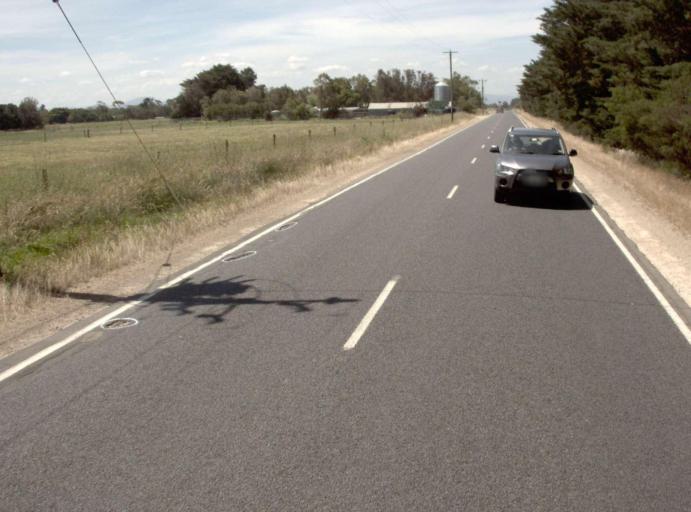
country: AU
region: Victoria
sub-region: Wellington
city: Heyfield
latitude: -38.0306
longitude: 146.8793
